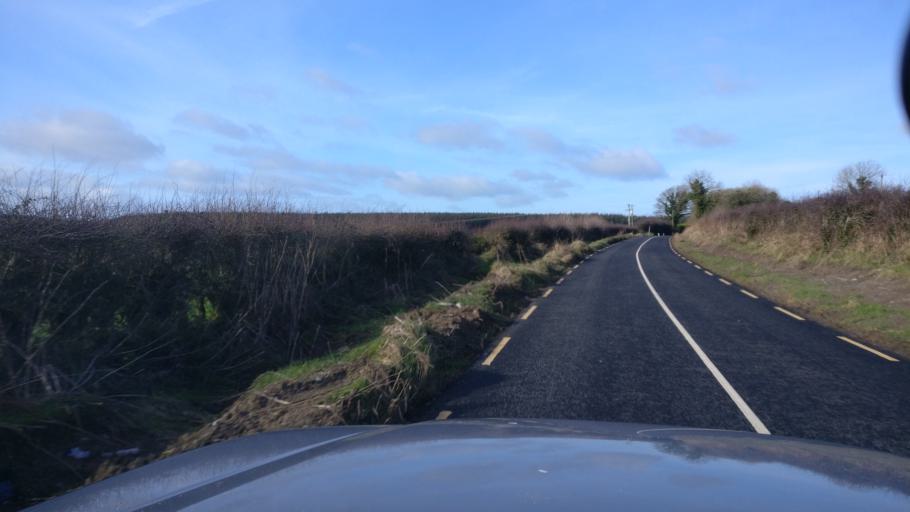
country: IE
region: Leinster
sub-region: Kilkenny
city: Castlecomer
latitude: 52.9053
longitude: -7.1818
